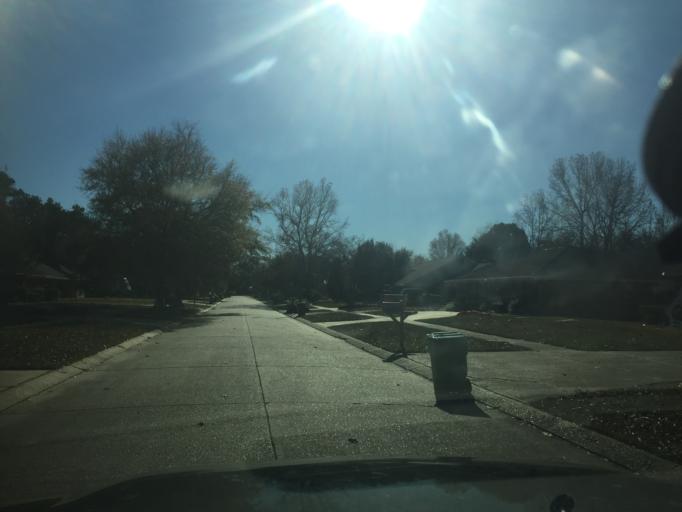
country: US
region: Louisiana
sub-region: Saint Tammany Parish
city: Slidell
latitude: 30.3027
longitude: -89.7458
